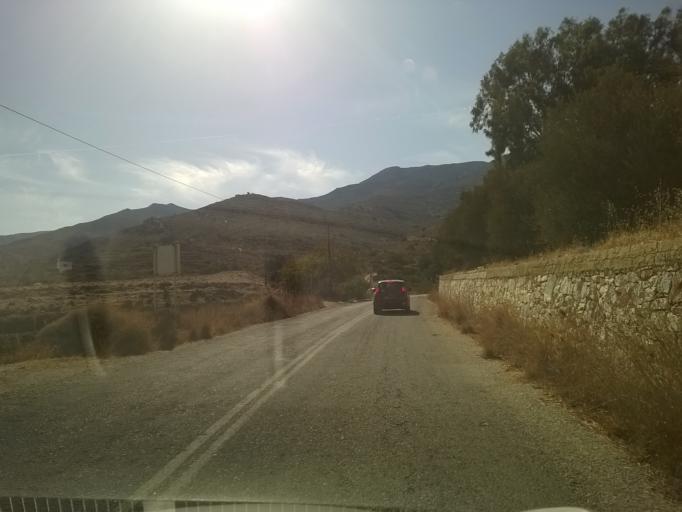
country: GR
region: South Aegean
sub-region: Nomos Kykladon
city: Filotion
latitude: 37.1753
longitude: 25.5486
